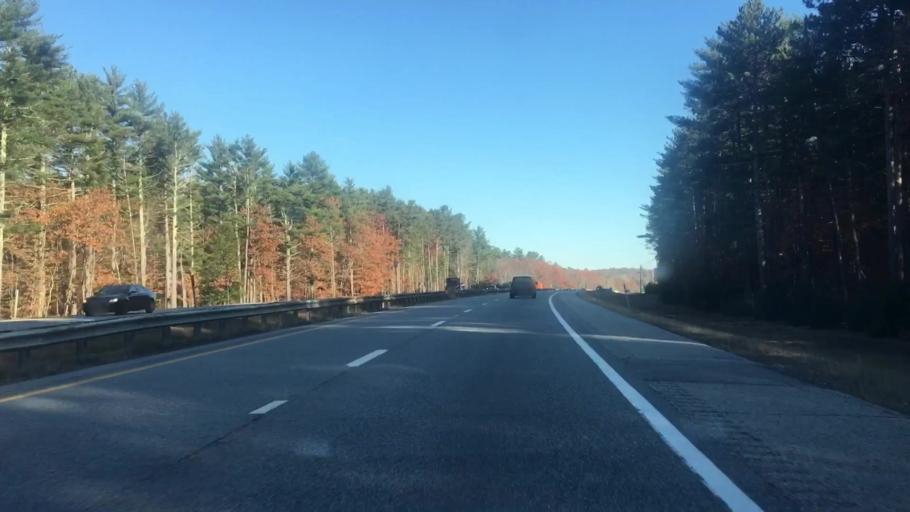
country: US
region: Maine
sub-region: Cumberland County
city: New Gloucester
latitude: 43.9946
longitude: -70.3091
